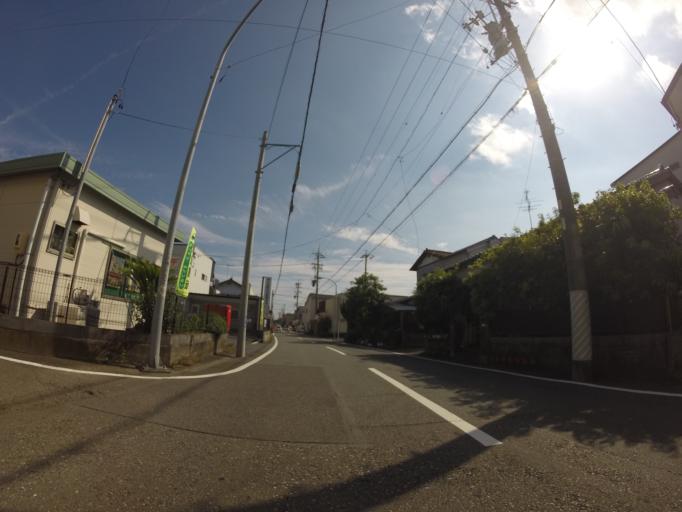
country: JP
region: Shizuoka
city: Shizuoka-shi
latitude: 35.0171
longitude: 138.4699
